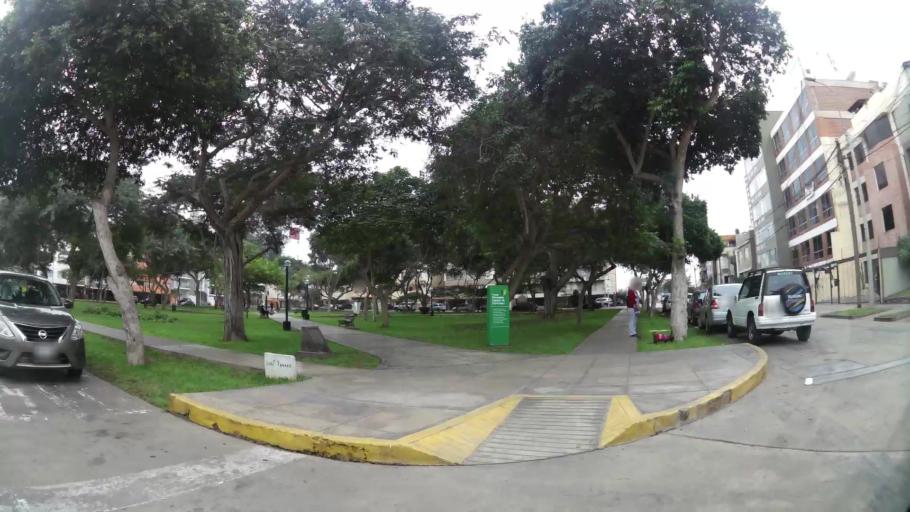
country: PE
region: Lima
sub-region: Lima
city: San Isidro
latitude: -12.1056
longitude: -77.0288
